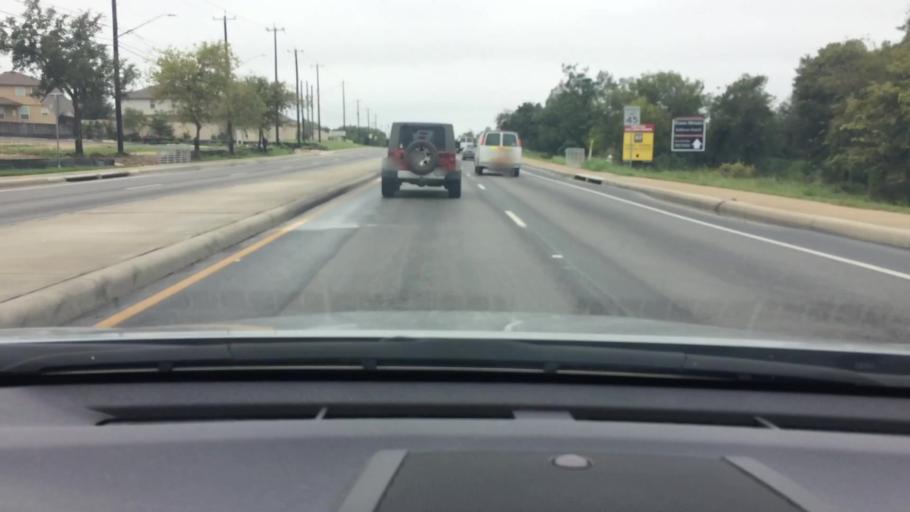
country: US
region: Texas
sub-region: Bexar County
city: Helotes
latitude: 29.5039
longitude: -98.7301
